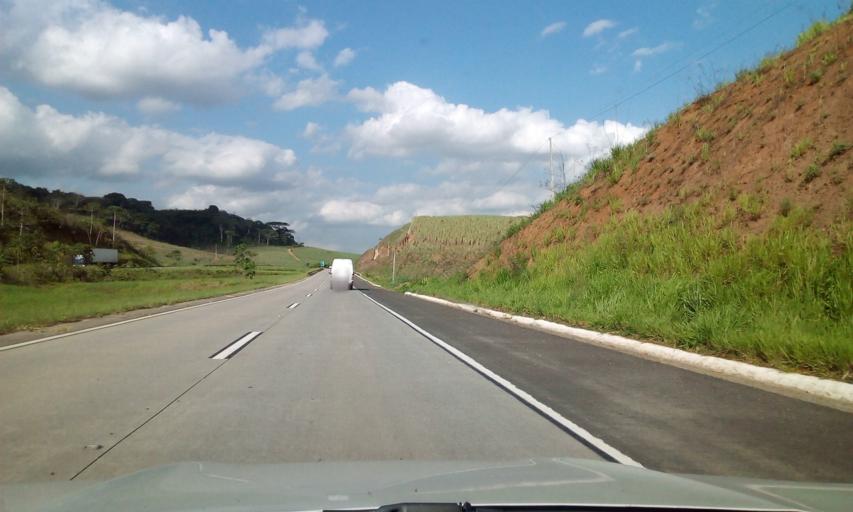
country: BR
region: Pernambuco
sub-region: Joaquim Nabuco
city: Joaquim Nabuco
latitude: -8.6068
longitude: -35.5407
